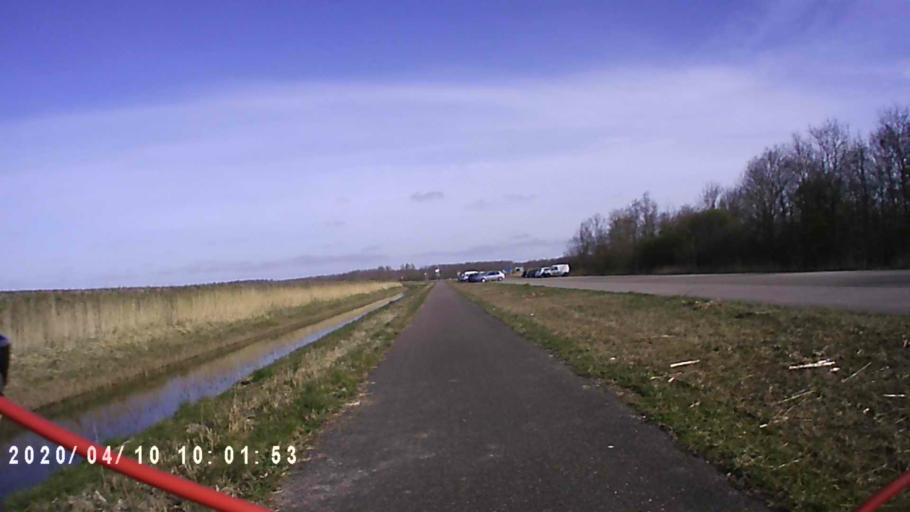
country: NL
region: Groningen
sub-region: Gemeente De Marne
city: Ulrum
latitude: 53.3631
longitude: 6.2605
